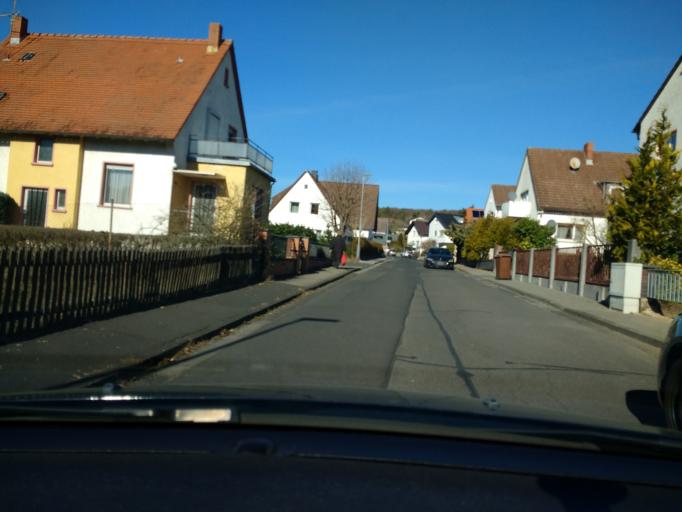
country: DE
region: Hesse
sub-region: Regierungsbezirk Darmstadt
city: Rodenbach
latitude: 50.1390
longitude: 9.0636
